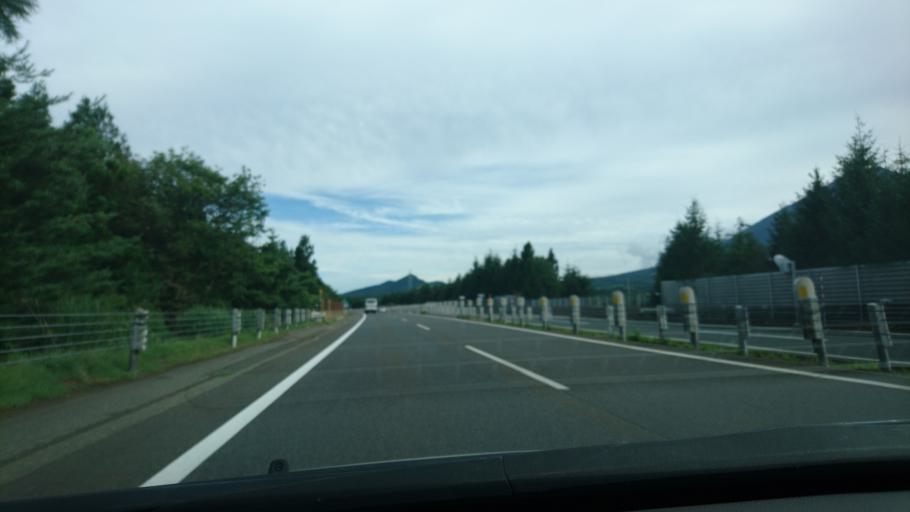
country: JP
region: Iwate
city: Shizukuishi
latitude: 39.9241
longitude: 141.0348
